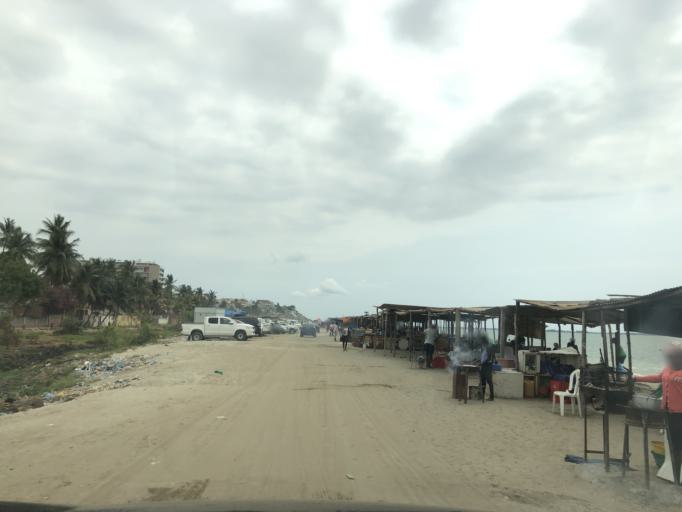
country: AO
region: Luanda
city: Luanda
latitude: -8.8739
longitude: 13.1917
